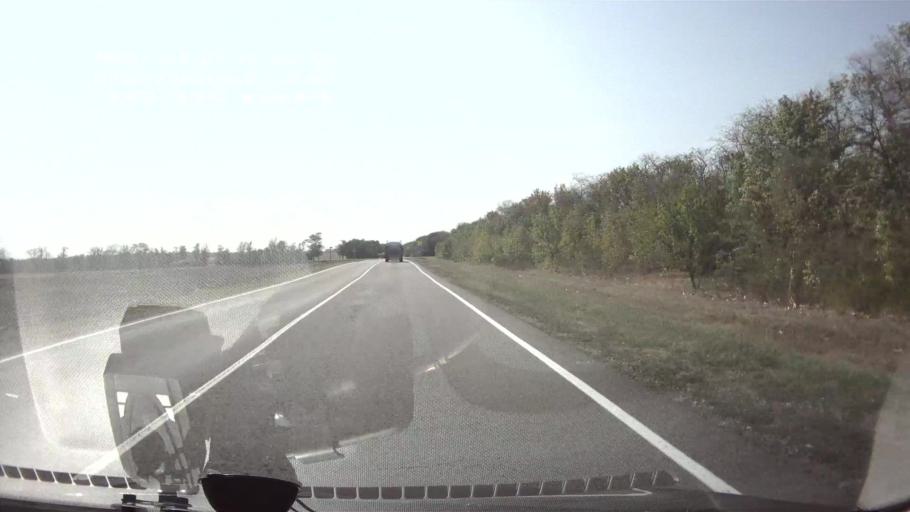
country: RU
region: Krasnodarskiy
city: Novopokrovskaya
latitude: 45.8209
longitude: 40.7201
